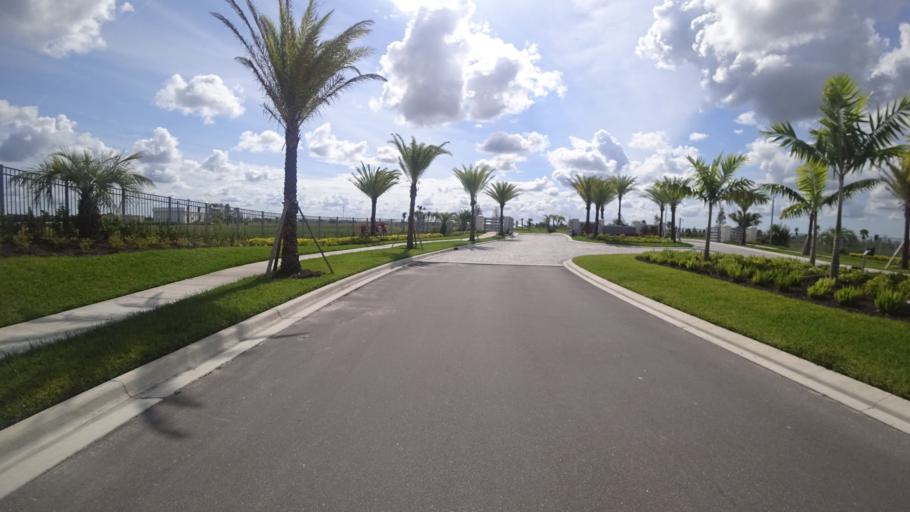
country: US
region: Florida
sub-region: Sarasota County
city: The Meadows
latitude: 27.4014
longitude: -82.3621
